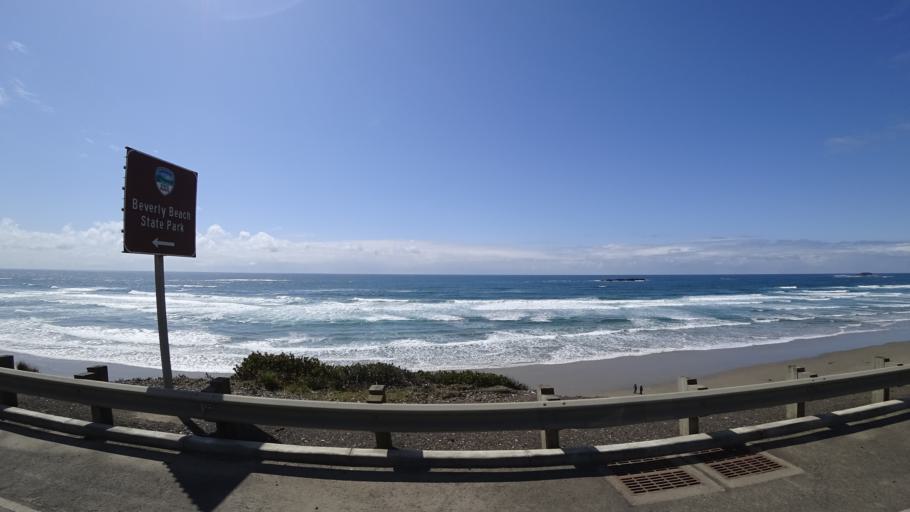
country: US
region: Oregon
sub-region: Lincoln County
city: Depoe Bay
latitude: 44.7266
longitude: -124.0578
